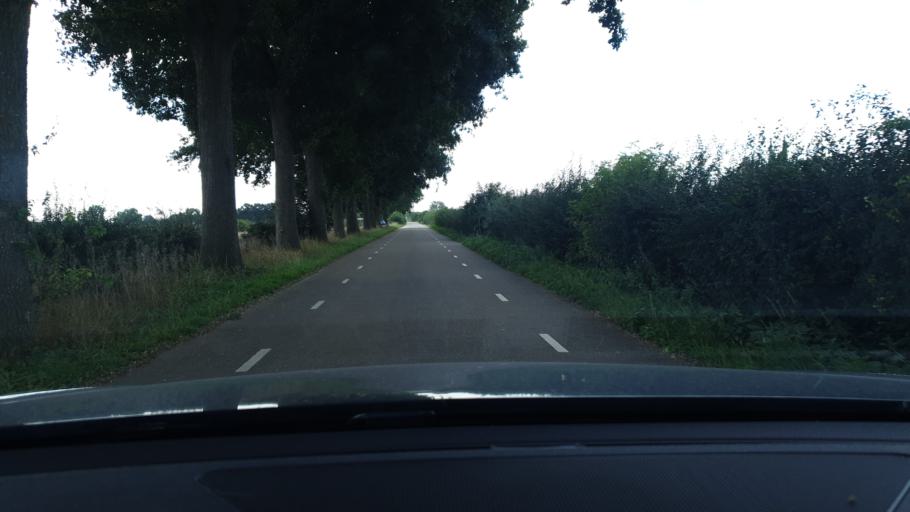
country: NL
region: North Brabant
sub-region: Gemeente Cuijk
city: Cuijk
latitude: 51.7343
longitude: 5.8864
